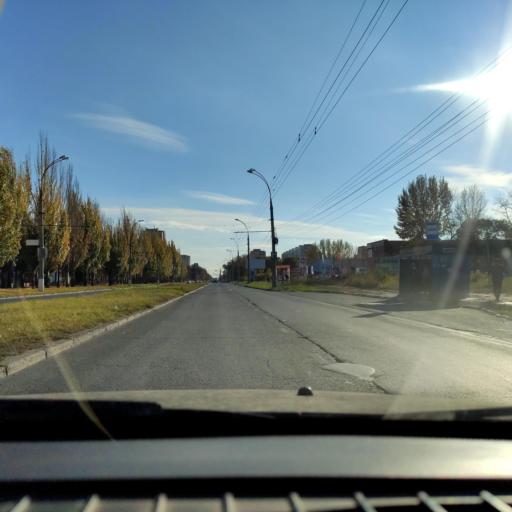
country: RU
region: Samara
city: Tol'yatti
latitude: 53.5413
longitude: 49.2791
